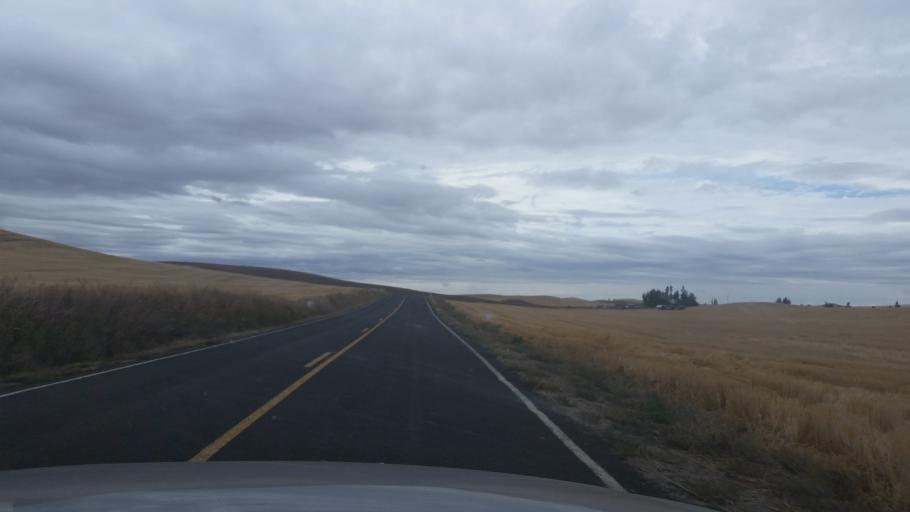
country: US
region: Washington
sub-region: Spokane County
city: Medical Lake
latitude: 47.5241
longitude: -117.8623
